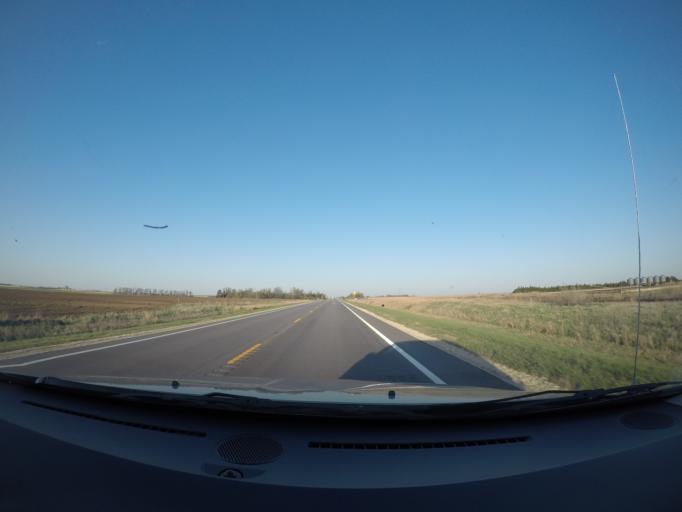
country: US
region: Kansas
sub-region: Stafford County
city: Stafford
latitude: 37.7980
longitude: -98.4618
